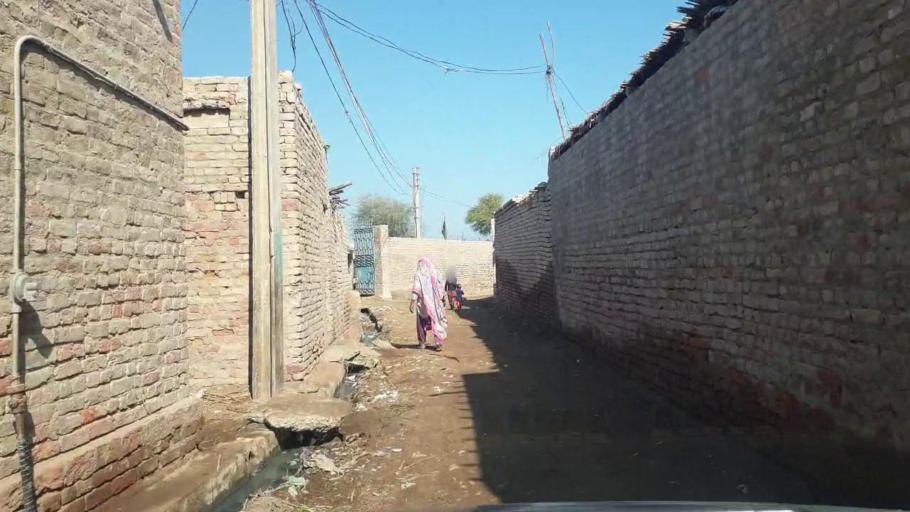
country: PK
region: Sindh
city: Shahdadpur
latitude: 25.8960
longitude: 68.5283
